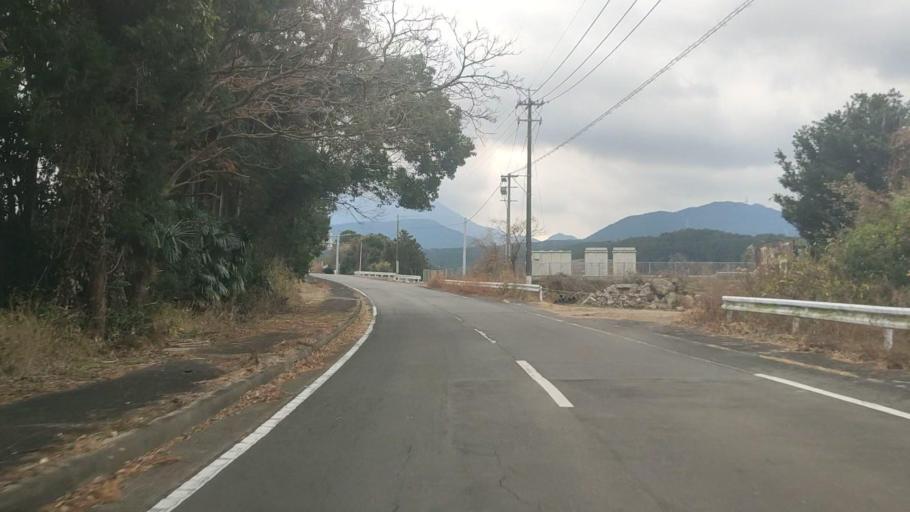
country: JP
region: Nagasaki
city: Shimabara
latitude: 32.8227
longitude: 130.2909
